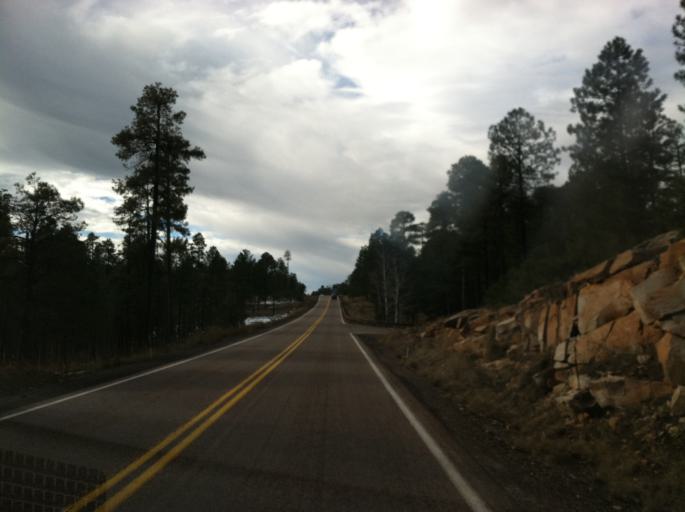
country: US
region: Arizona
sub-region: Navajo County
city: Heber-Overgaard
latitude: 34.3203
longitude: -110.8447
